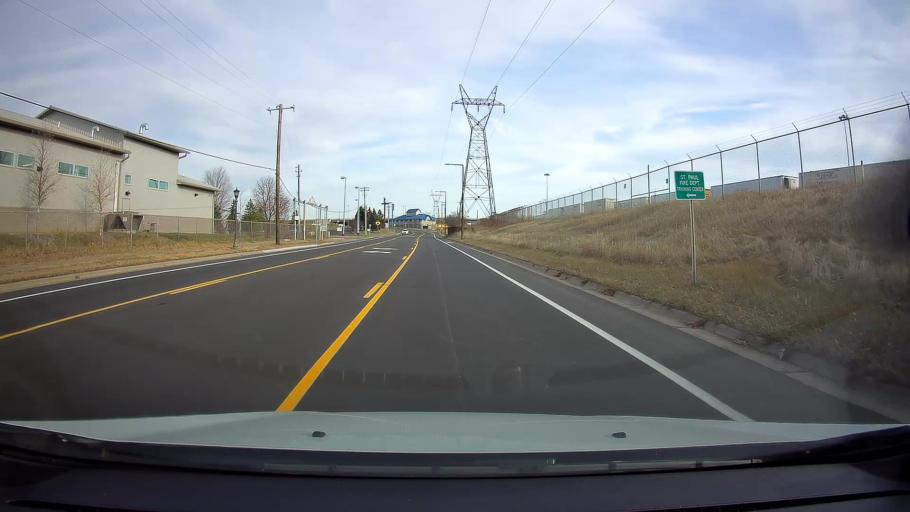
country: US
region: Minnesota
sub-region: Ramsey County
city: Falcon Heights
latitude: 44.9712
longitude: -93.1717
